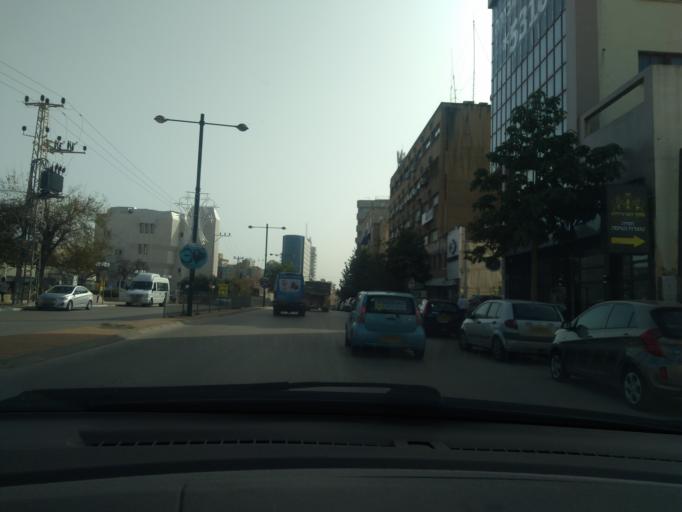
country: IL
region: Central District
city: Netanya
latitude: 32.3286
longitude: 34.8619
